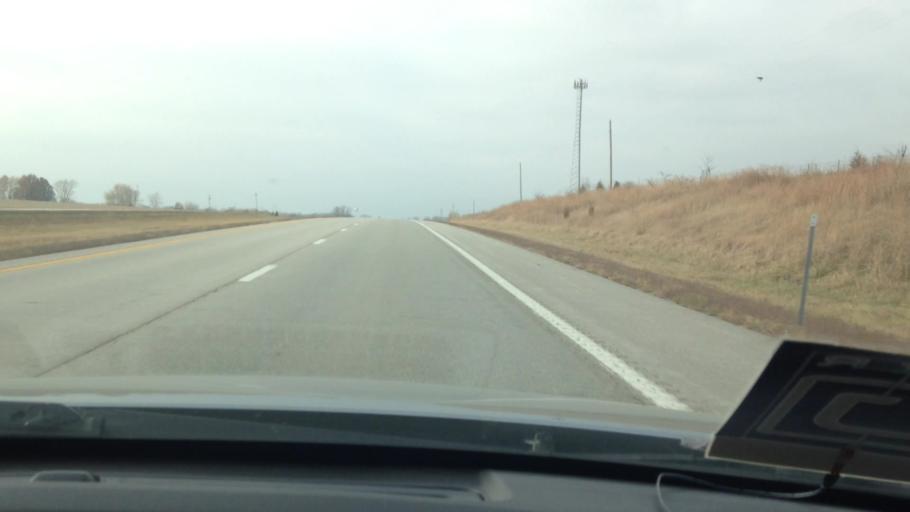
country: US
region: Missouri
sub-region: Cass County
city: Garden City
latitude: 38.5488
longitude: -94.1718
